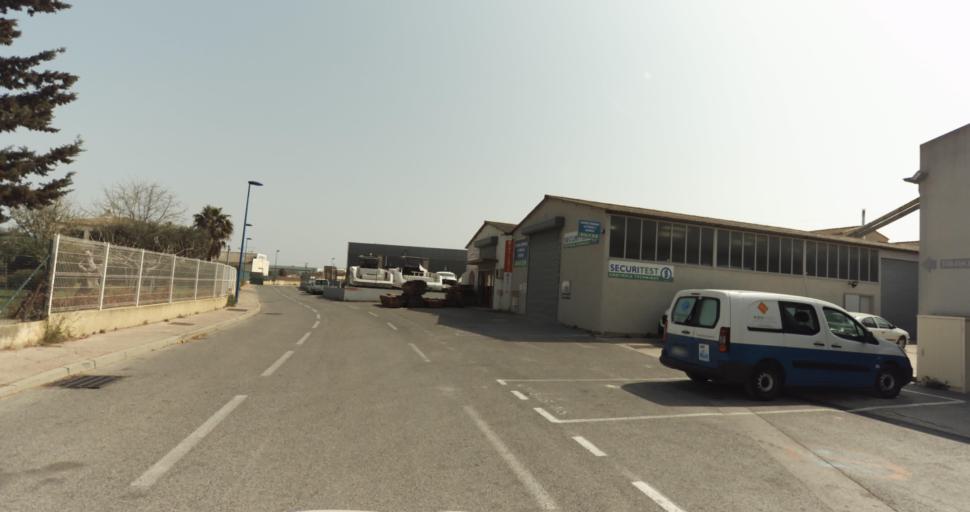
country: FR
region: Provence-Alpes-Cote d'Azur
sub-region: Departement du Var
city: Bormes-les-Mimosas
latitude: 43.1324
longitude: 6.3476
